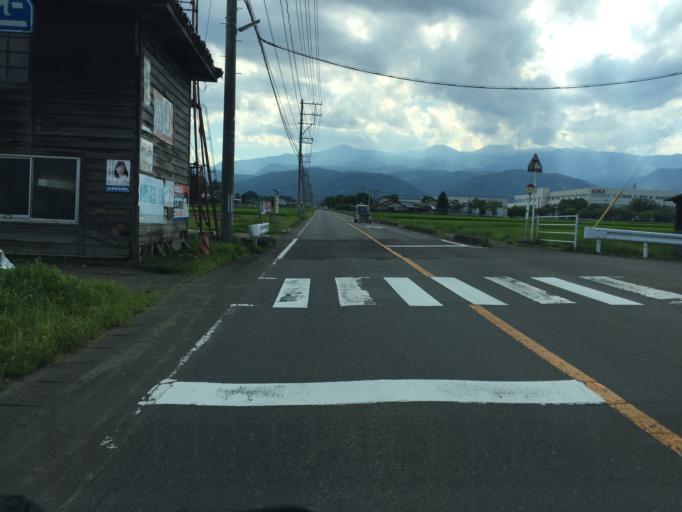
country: JP
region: Fukushima
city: Fukushima-shi
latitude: 37.7477
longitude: 140.3998
